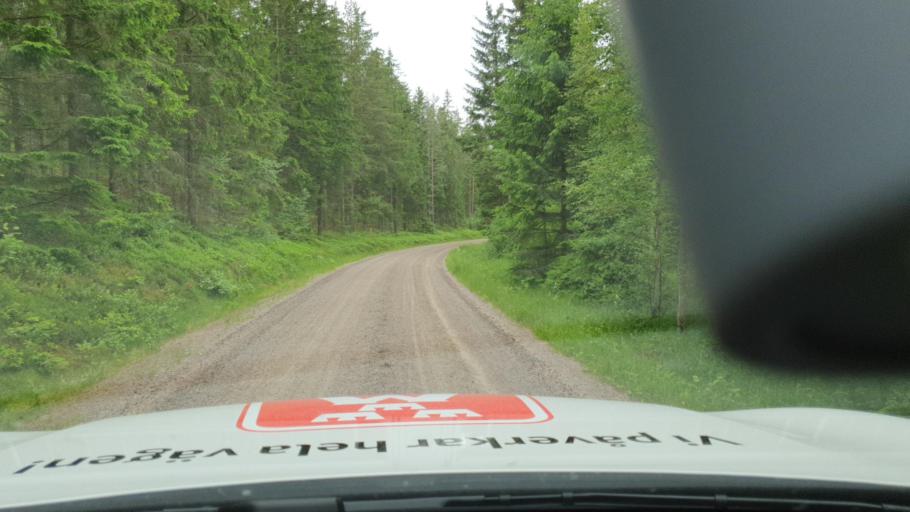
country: SE
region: Vaestra Goetaland
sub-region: Hjo Kommun
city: Hjo
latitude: 58.3466
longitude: 14.3166
